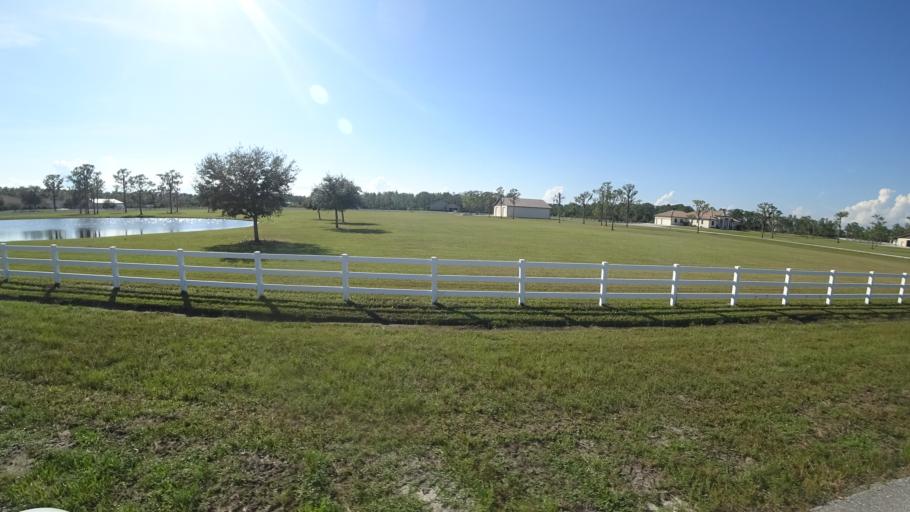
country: US
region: Florida
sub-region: Sarasota County
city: Lake Sarasota
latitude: 27.3949
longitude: -82.2835
